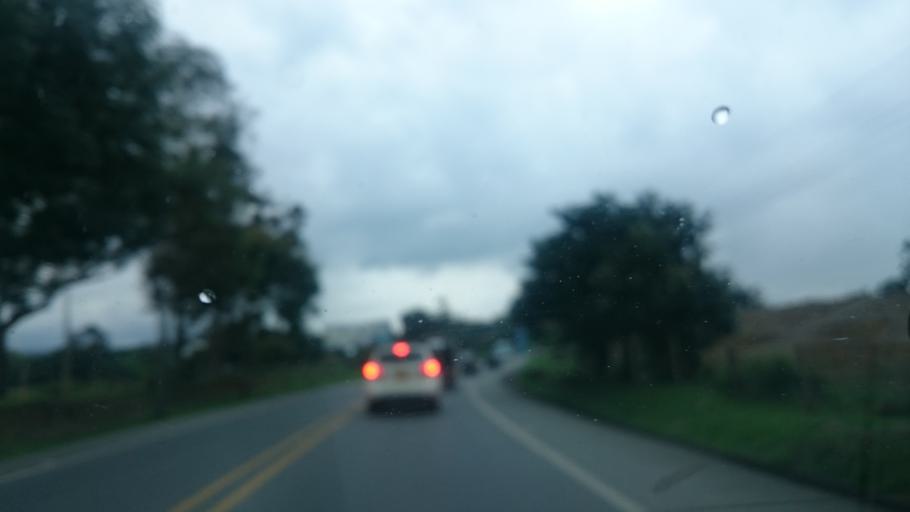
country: CO
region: Cauca
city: Popayan
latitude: 2.5164
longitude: -76.5430
